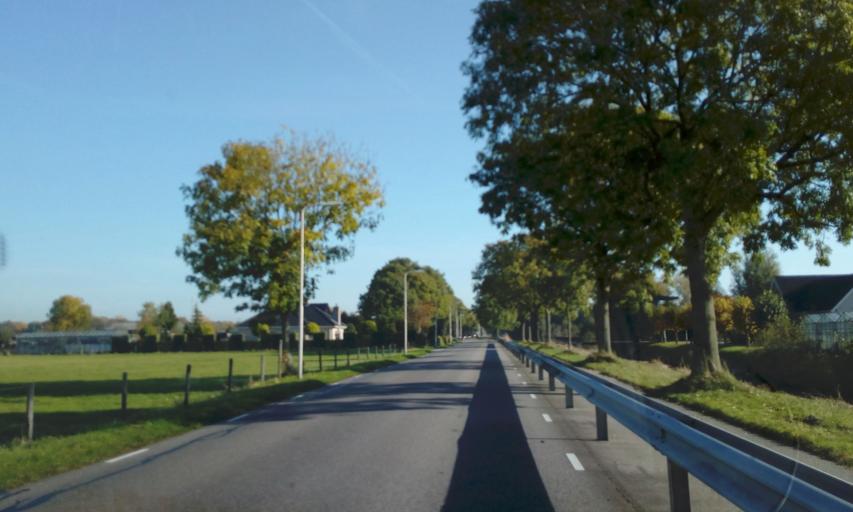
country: NL
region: South Holland
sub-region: Gemeente Lansingerland
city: Bleiswijk
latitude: 52.0021
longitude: 4.5307
